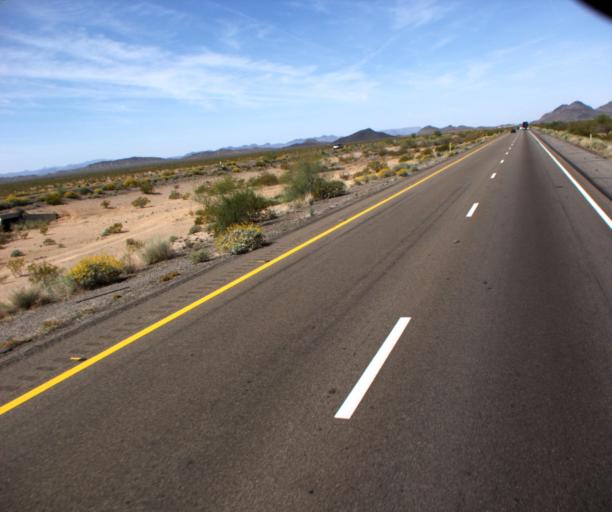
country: US
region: Arizona
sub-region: La Paz County
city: Salome
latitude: 33.6003
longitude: -113.5594
